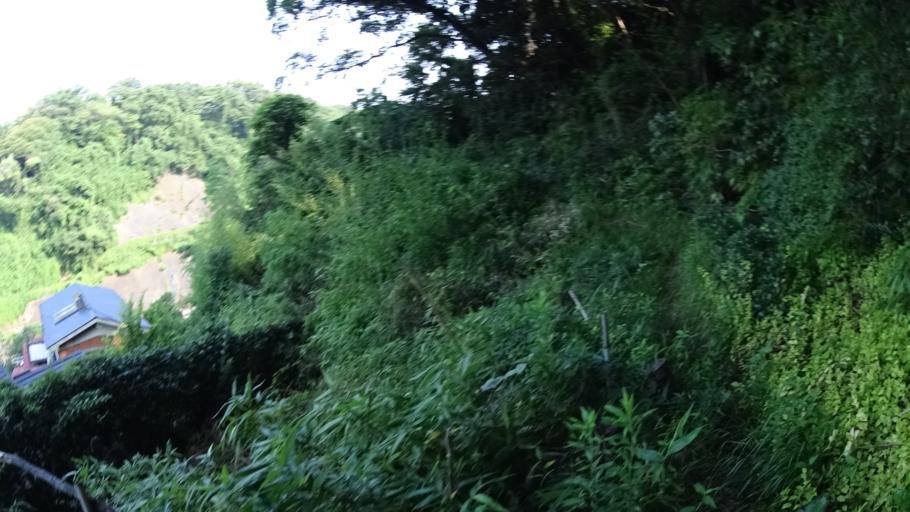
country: JP
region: Kanagawa
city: Yokosuka
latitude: 35.3028
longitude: 139.6260
